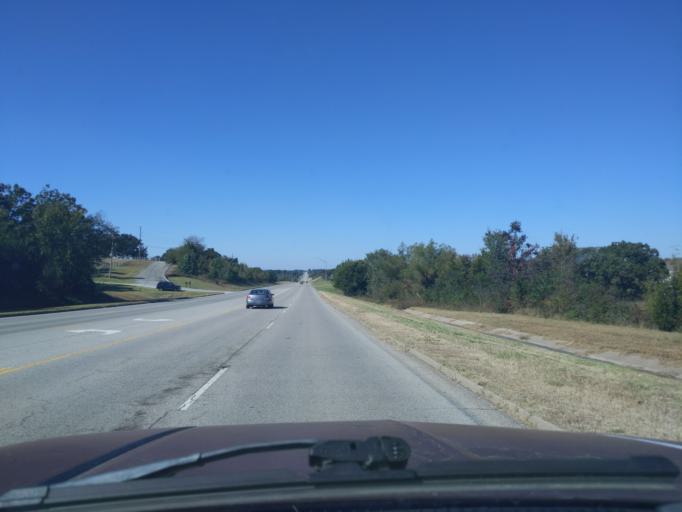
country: US
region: Oklahoma
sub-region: Creek County
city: Kiefer
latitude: 35.9885
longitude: -96.0501
